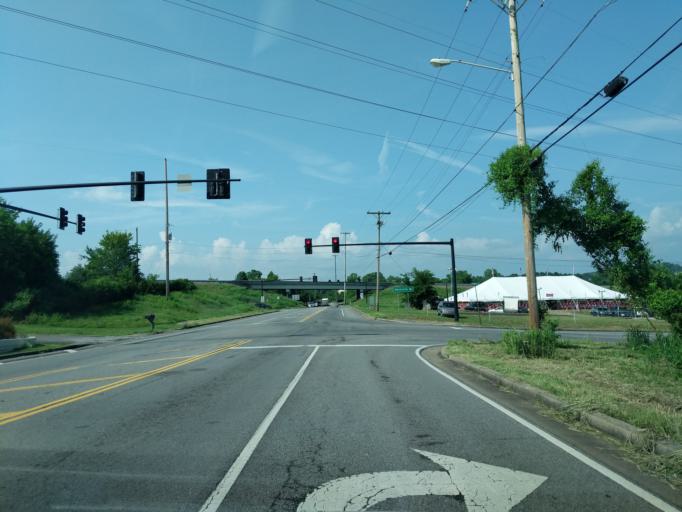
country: US
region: Tennessee
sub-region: Sumner County
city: Hendersonville
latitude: 36.3142
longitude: -86.6638
